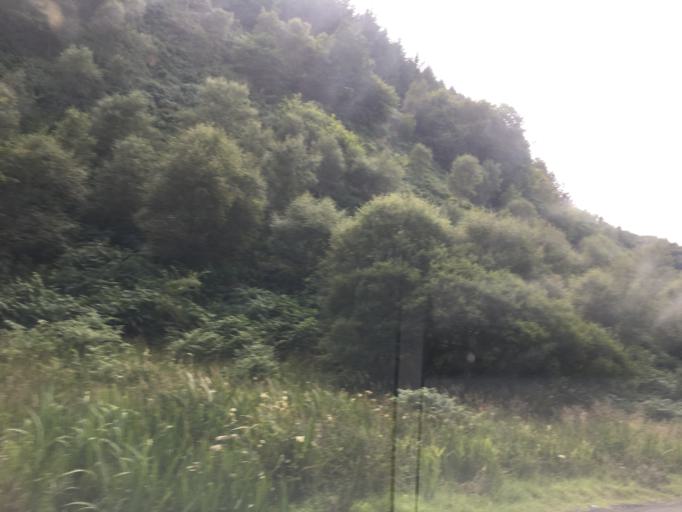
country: GB
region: Scotland
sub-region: Argyll and Bute
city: Ardrishaig
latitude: 56.0852
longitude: -5.5598
